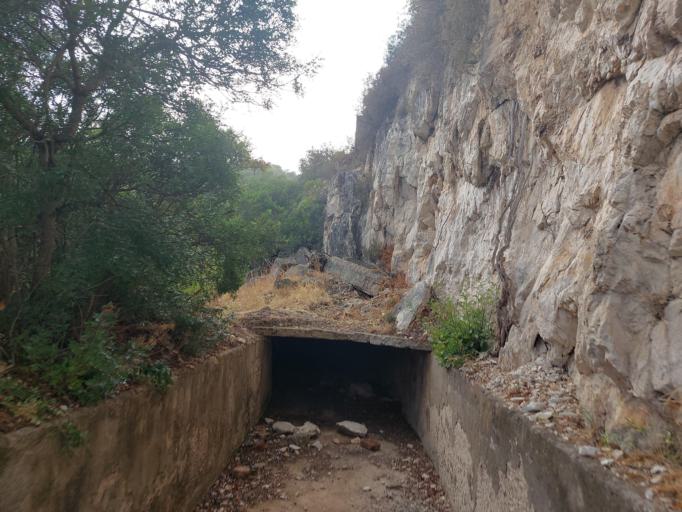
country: HR
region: Dubrovacko-Neretvanska
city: Smokvica
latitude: 42.7441
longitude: 16.8265
